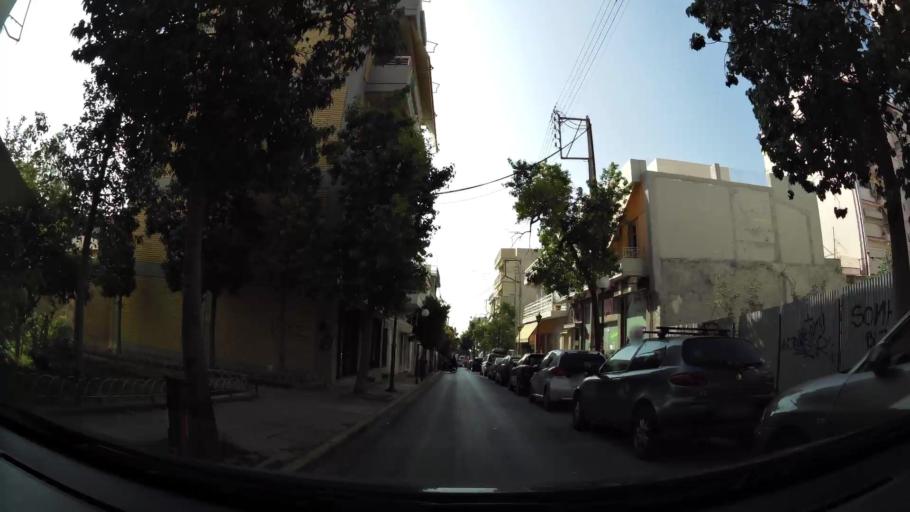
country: GR
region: Attica
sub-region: Nomos Piraios
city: Drapetsona
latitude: 37.9487
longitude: 23.6263
